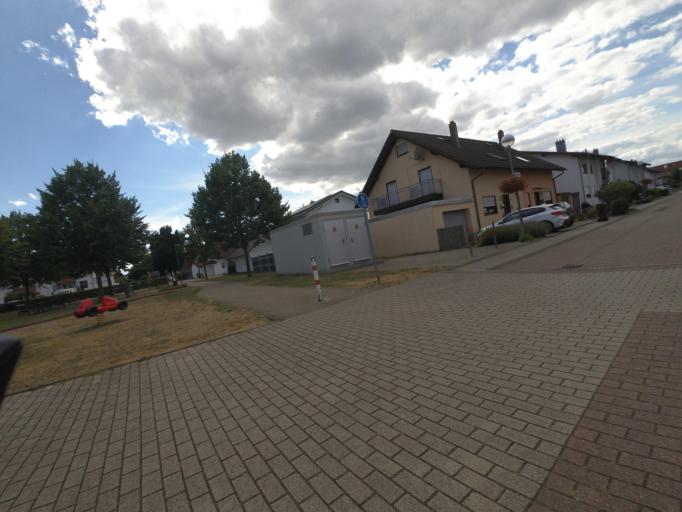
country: DE
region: Baden-Wuerttemberg
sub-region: Karlsruhe Region
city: Sinzheim
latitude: 48.7739
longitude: 8.1650
